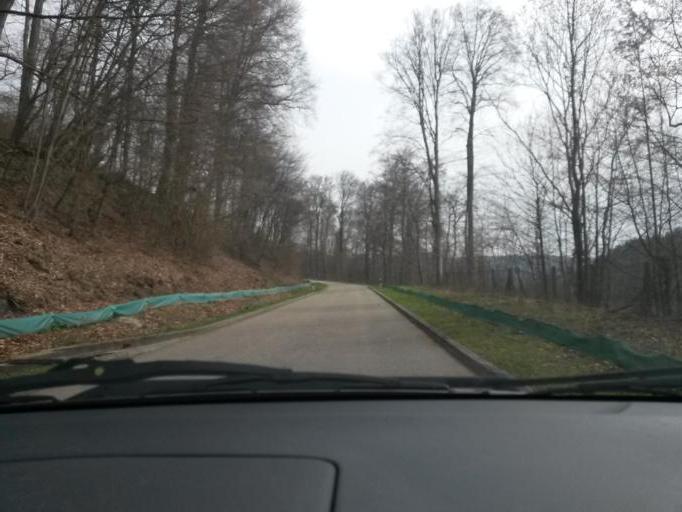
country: DE
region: Baden-Wuerttemberg
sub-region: Freiburg Region
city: Lahr
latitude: 48.3086
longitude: 7.8677
